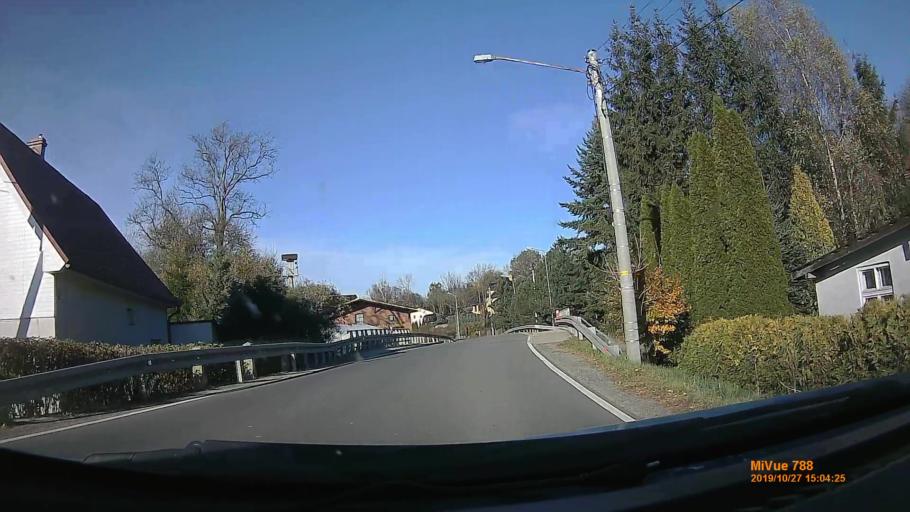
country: PL
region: Lower Silesian Voivodeship
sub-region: Powiat klodzki
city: Miedzylesie
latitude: 50.1404
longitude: 16.6629
